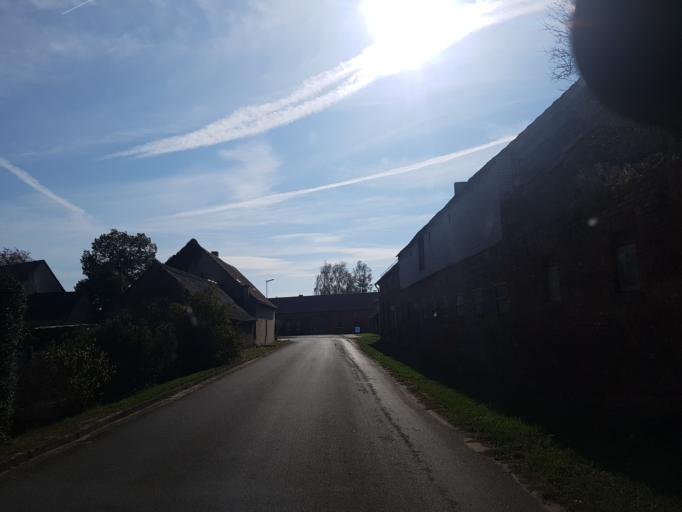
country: DE
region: Brandenburg
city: Ihlow
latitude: 51.8328
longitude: 13.3431
